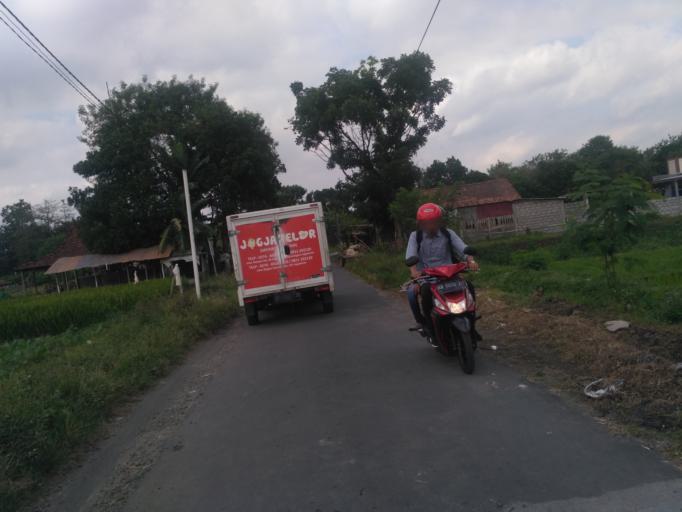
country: ID
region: Daerah Istimewa Yogyakarta
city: Melati
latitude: -7.7509
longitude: 110.3556
